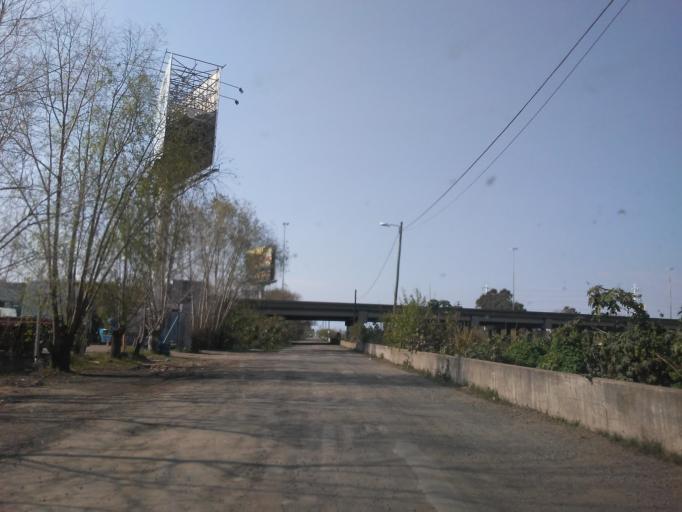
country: AR
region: Buenos Aires
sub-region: Partido de Avellaneda
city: Avellaneda
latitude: -34.6820
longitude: -58.3172
